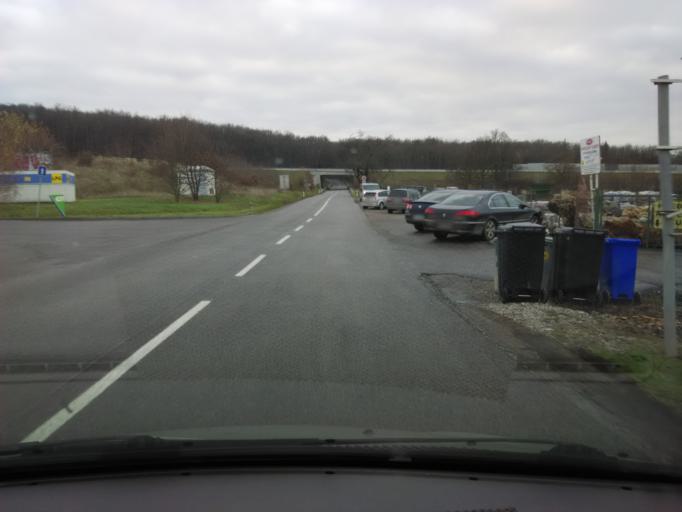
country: SK
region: Nitriansky
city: Tlmace
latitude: 48.3544
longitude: 18.4794
